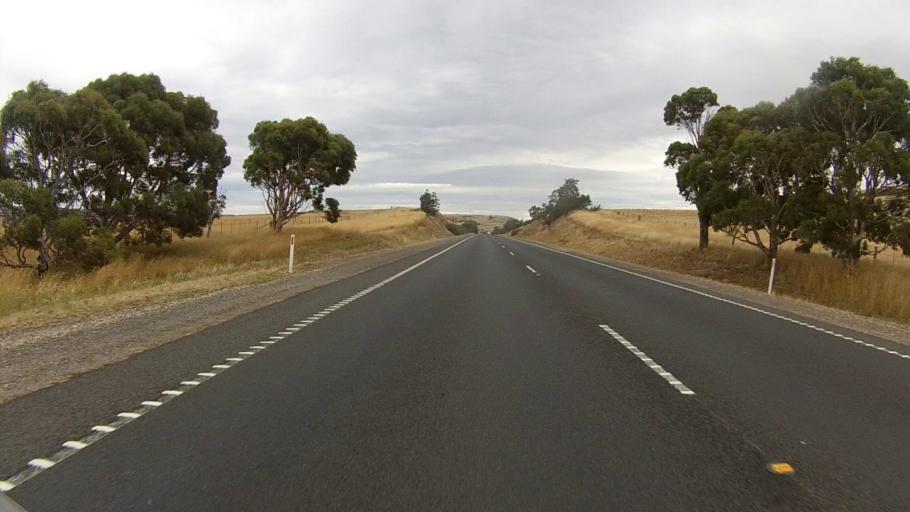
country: AU
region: Tasmania
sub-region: Brighton
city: Bridgewater
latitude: -42.3540
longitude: 147.3369
